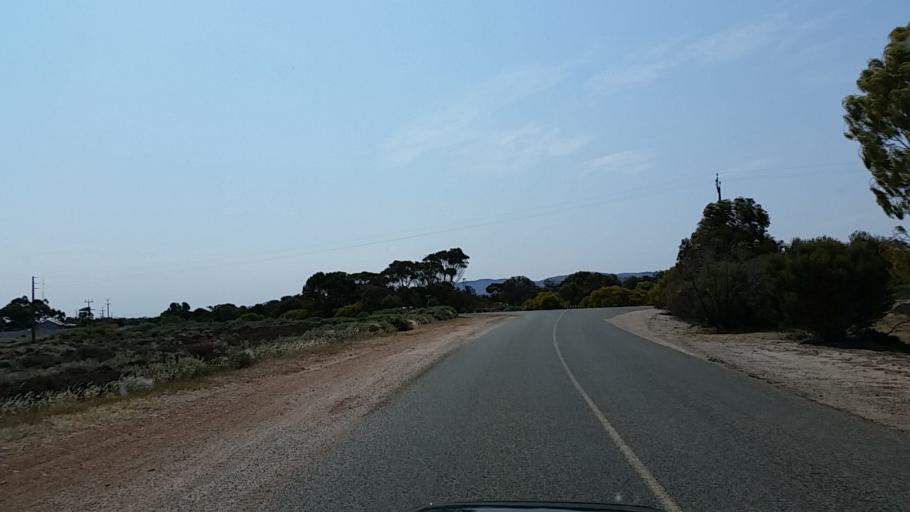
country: AU
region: South Australia
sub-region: Port Pirie City and Dists
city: Port Pirie
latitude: -33.0157
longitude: 138.0013
